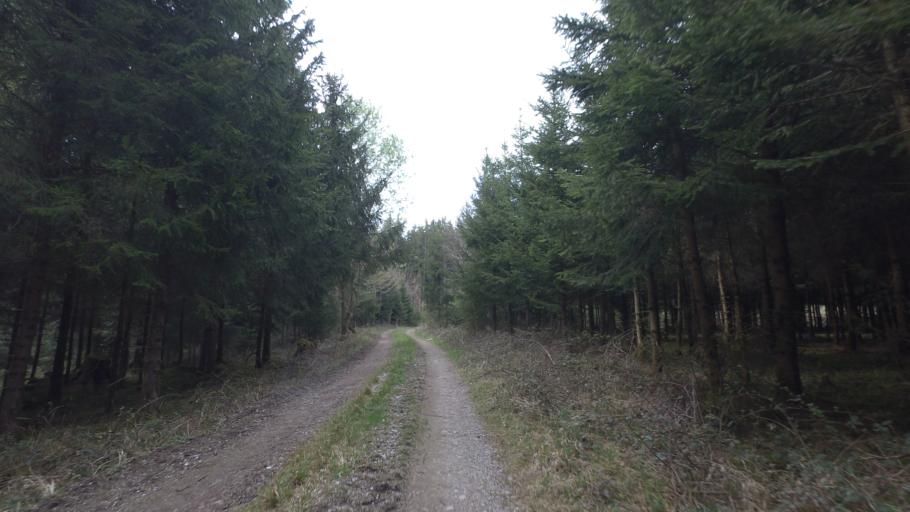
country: DE
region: Bavaria
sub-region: Upper Bavaria
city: Nussdorf
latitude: 47.9183
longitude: 12.5835
